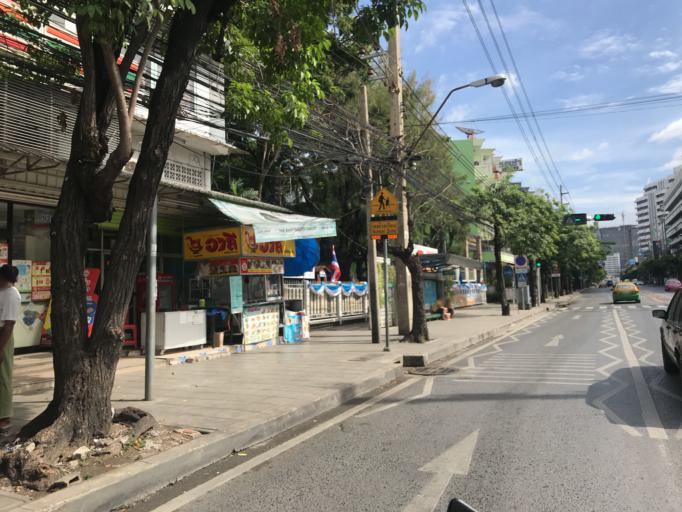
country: TH
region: Bangkok
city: Watthana
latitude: 13.7305
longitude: 100.5965
